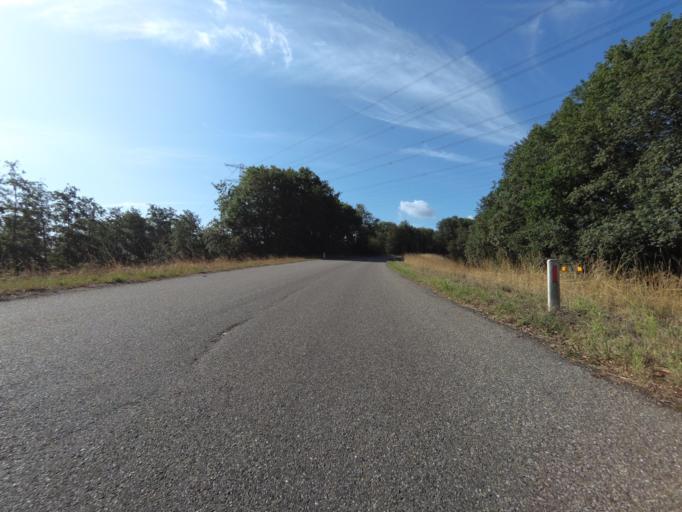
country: NL
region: Overijssel
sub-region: Gemeente Hengelo
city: Hengelo
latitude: 52.2288
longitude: 6.7884
